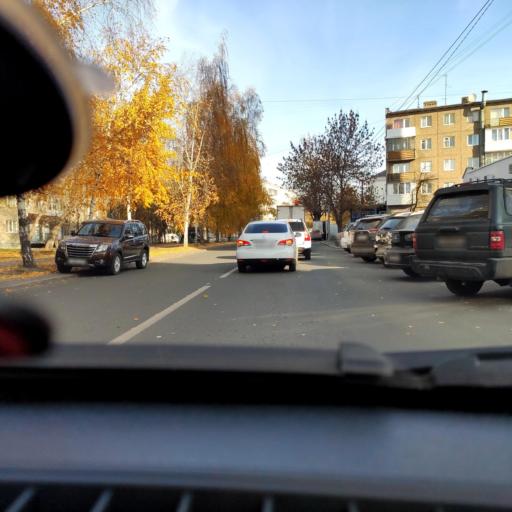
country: RU
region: Bashkortostan
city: Ufa
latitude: 54.7306
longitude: 55.9631
